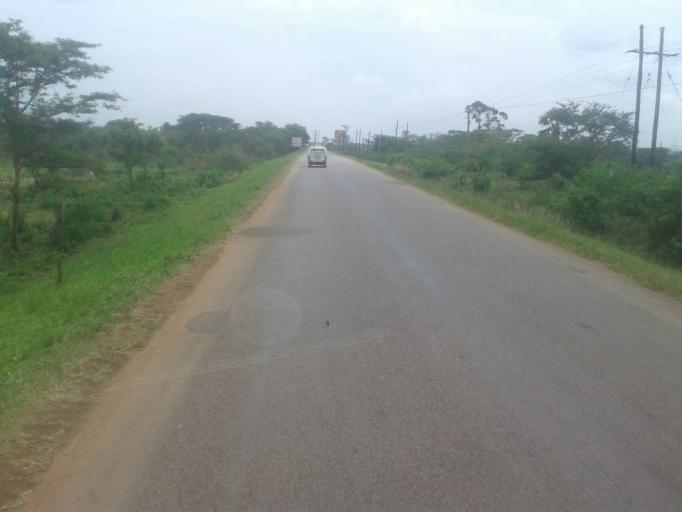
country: UG
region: Western Region
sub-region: Kiryandongo District
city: Masindi Port
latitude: 1.5370
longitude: 32.0423
